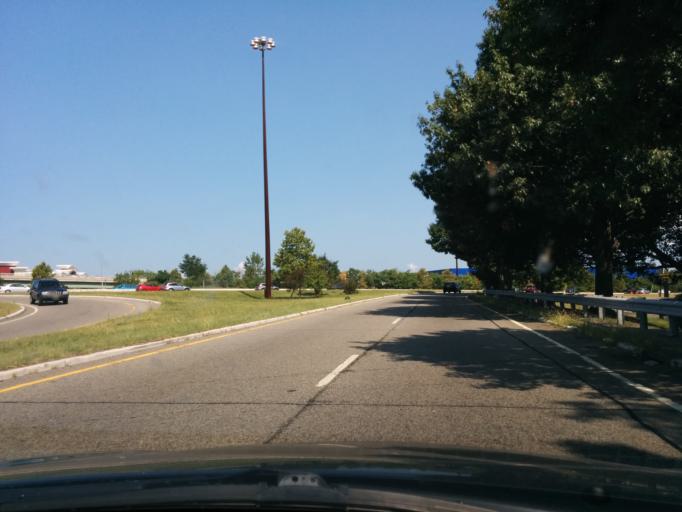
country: US
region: New Jersey
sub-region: Bergen County
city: Rochelle Park
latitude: 40.9213
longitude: -74.0710
